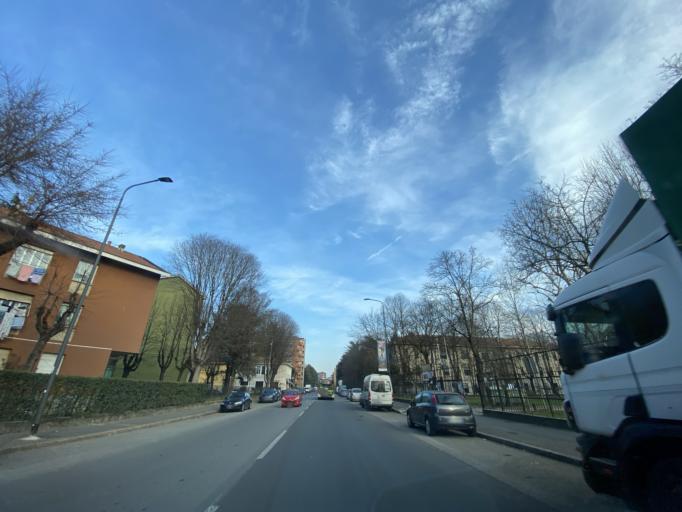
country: IT
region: Lombardy
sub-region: Citta metropolitana di Milano
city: Cormano
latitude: 45.5228
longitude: 9.1605
